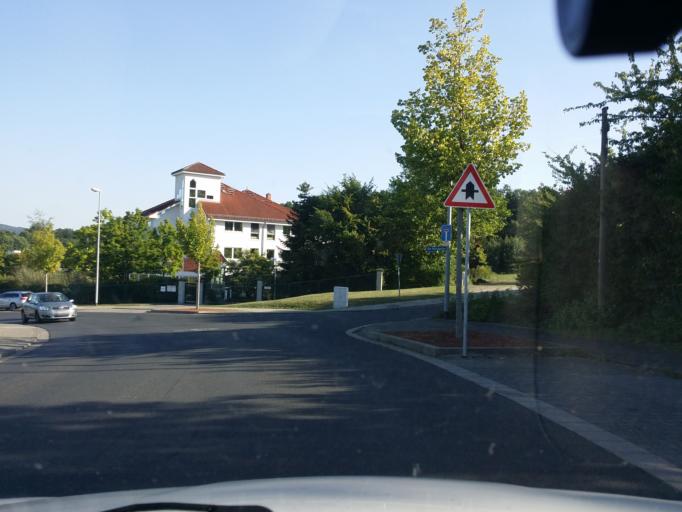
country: DE
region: Hesse
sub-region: Regierungsbezirk Darmstadt
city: Idstein
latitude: 50.2066
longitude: 8.2554
